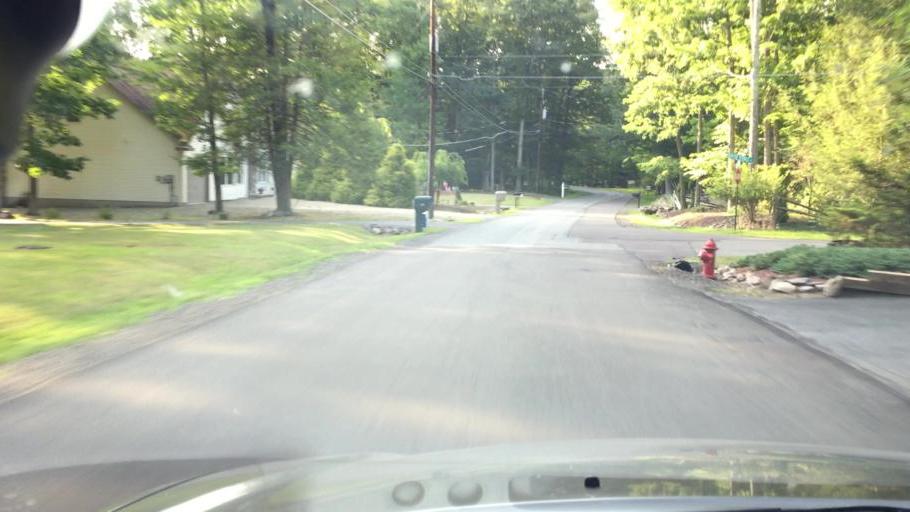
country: US
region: Pennsylvania
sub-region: Luzerne County
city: Freeland
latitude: 41.0380
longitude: -75.9372
